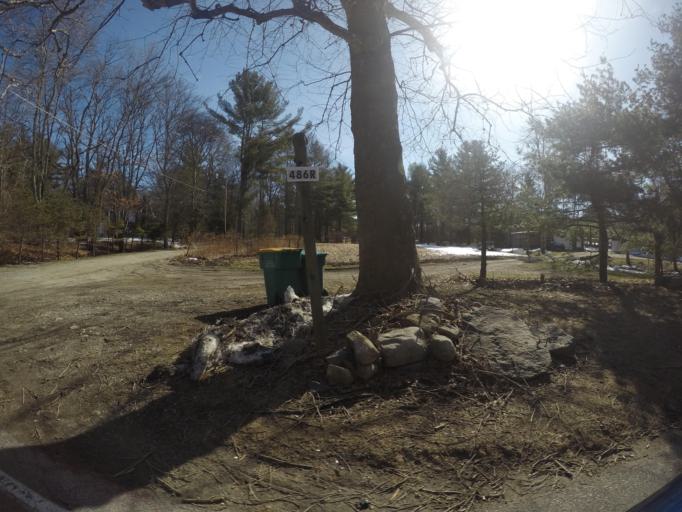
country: US
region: Massachusetts
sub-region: Bristol County
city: Easton
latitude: 42.0099
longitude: -71.1202
